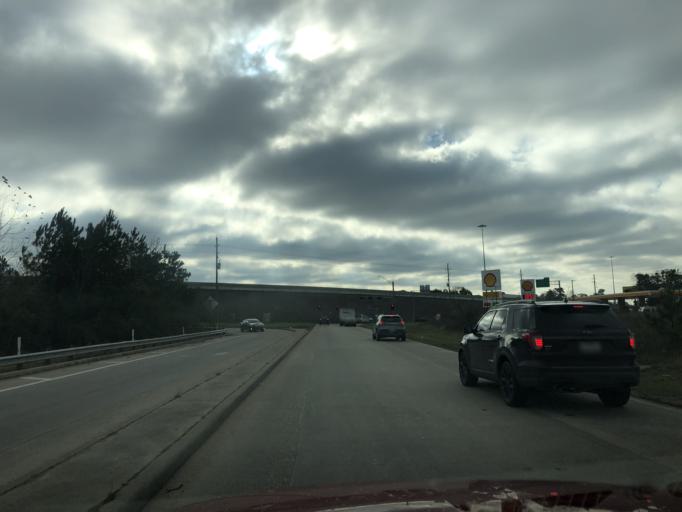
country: US
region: Texas
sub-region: Harris County
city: Spring
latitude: 30.0825
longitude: -95.4384
